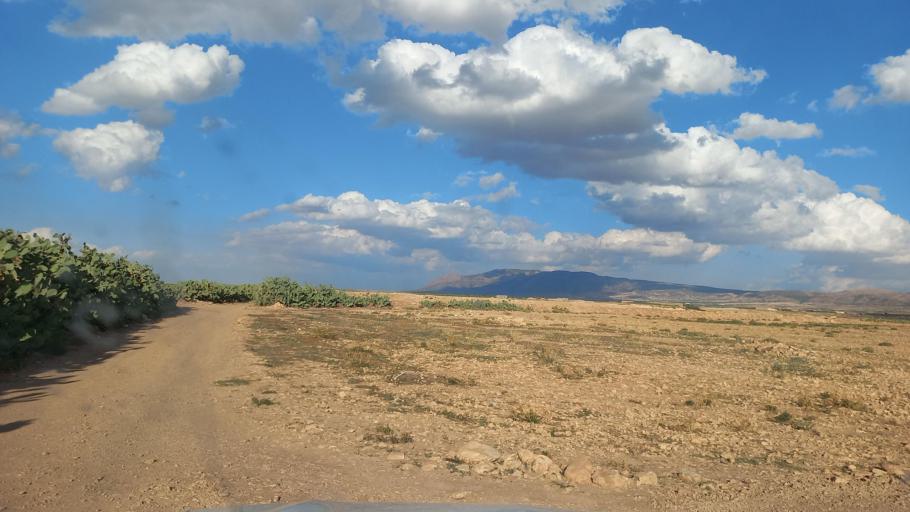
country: TN
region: Al Qasrayn
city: Sbiba
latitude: 35.3857
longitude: 9.0682
